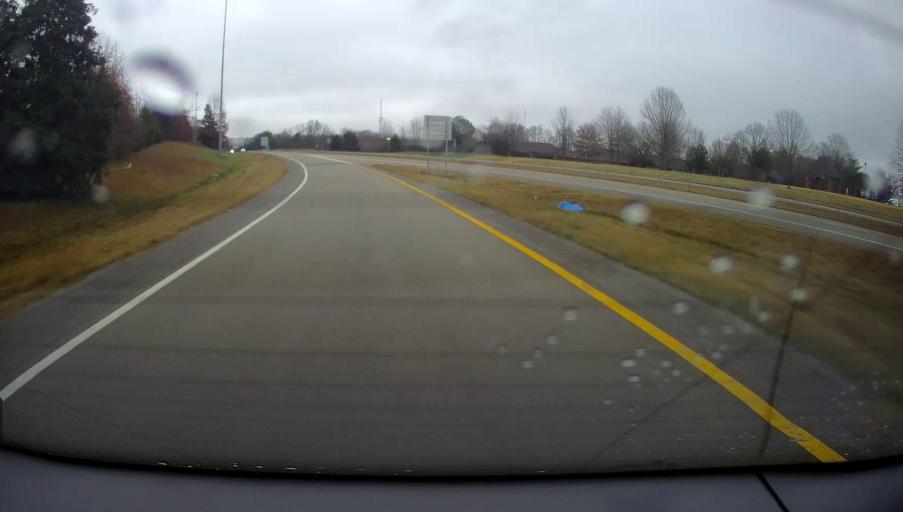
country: US
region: Mississippi
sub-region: Alcorn County
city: Corinth
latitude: 34.9108
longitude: -88.5442
